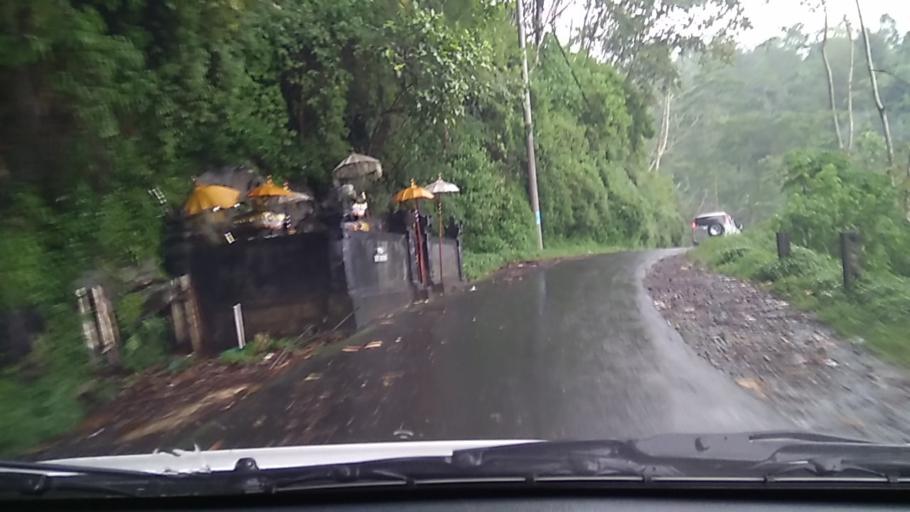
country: ID
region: Bali
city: Banjar Ambengan
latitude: -8.2234
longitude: 115.1602
